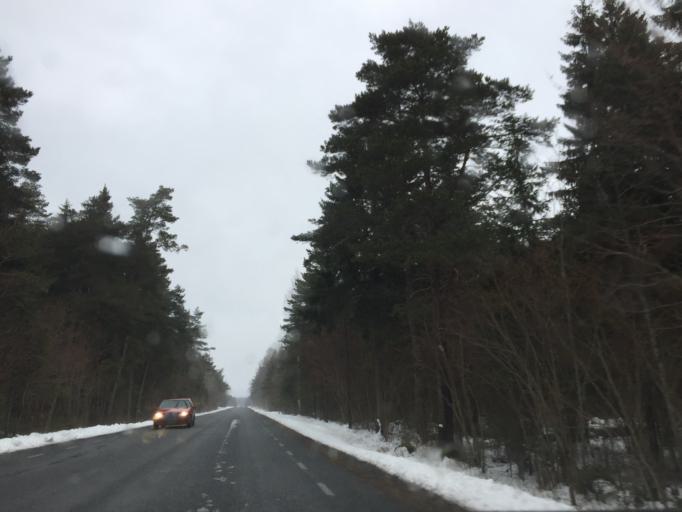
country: EE
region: Saare
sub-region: Kuressaare linn
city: Kuressaare
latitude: 58.3394
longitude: 22.0287
